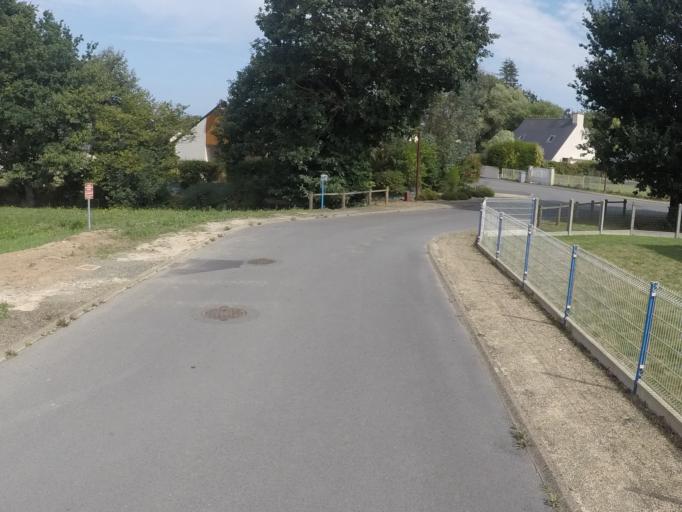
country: FR
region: Brittany
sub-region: Departement des Cotes-d'Armor
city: Goudelin
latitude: 48.6003
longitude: -3.0227
